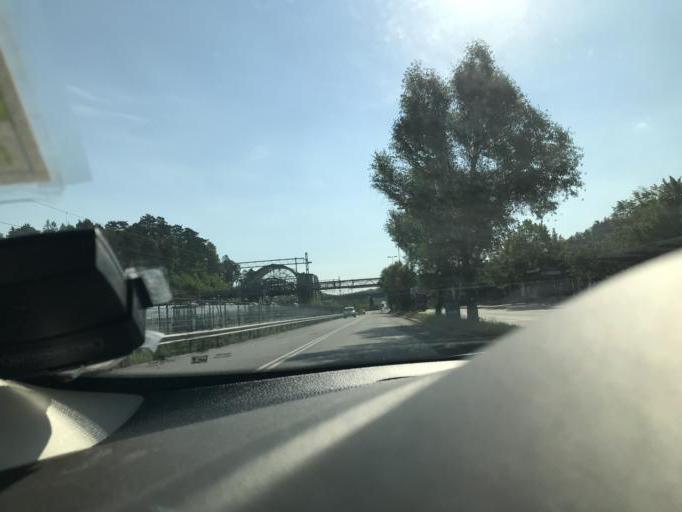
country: SE
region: Stockholm
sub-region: Botkyrka Kommun
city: Tumba
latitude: 59.1994
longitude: 17.8354
